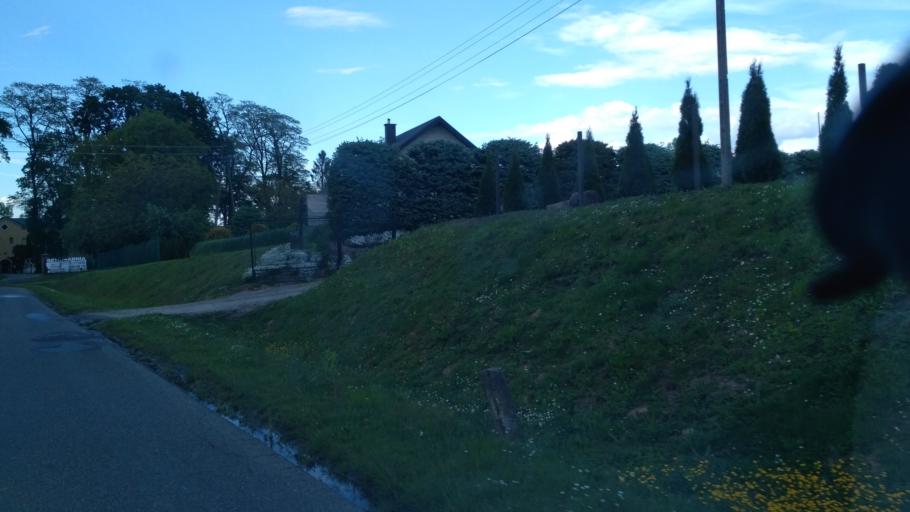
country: PL
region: Subcarpathian Voivodeship
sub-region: Powiat jaroslawski
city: Rokietnica
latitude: 49.9383
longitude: 22.6666
